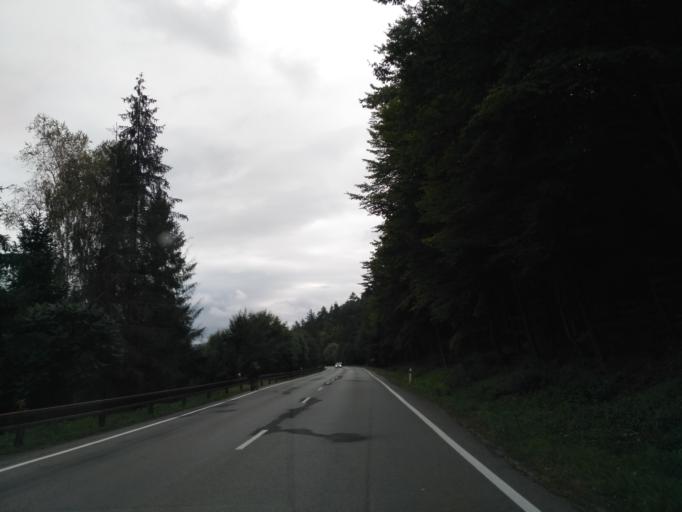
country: SK
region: Presovsky
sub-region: Okres Presov
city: Presov
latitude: 48.9786
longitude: 21.1729
